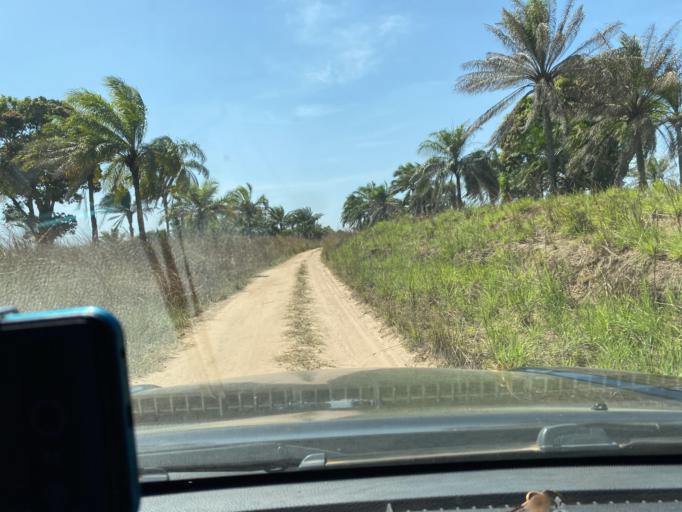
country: CD
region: Kasai-Oriental
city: Kabinda
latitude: -5.8872
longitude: 24.8478
